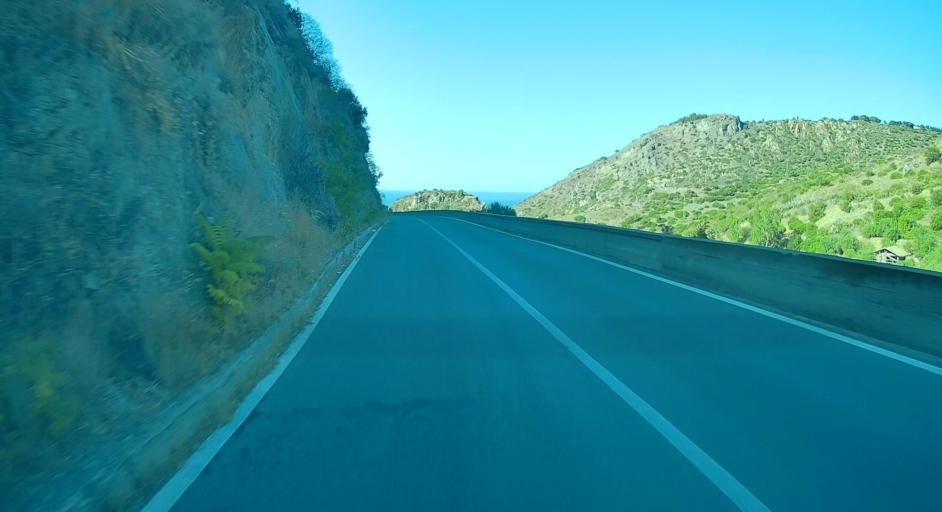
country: IT
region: Sicily
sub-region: Messina
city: Oliveri
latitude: 38.1376
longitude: 15.0331
